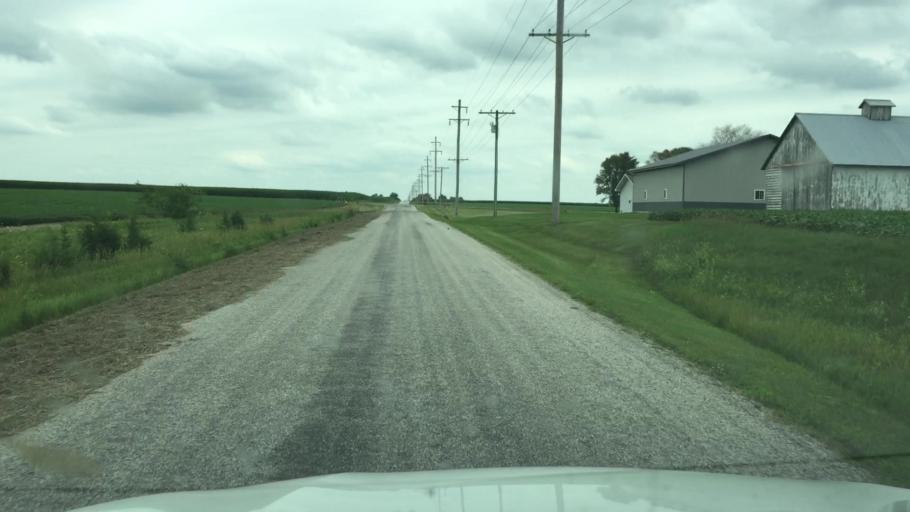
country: US
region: Illinois
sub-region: Hancock County
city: Carthage
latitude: 40.3435
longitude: -91.0823
